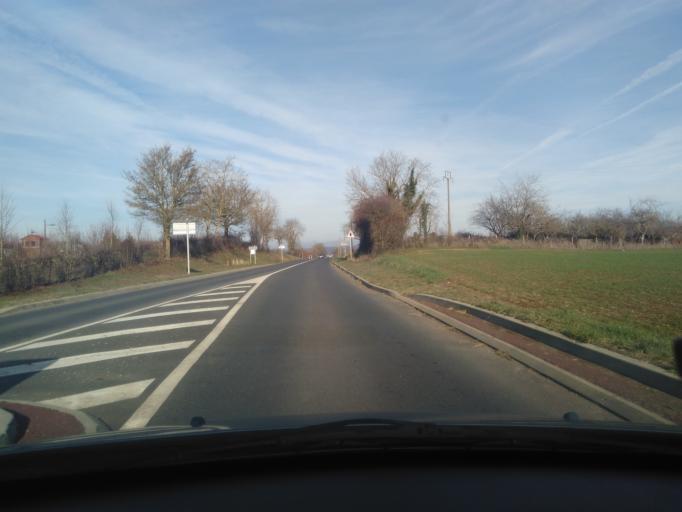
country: FR
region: Centre
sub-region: Departement du Cher
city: Orval
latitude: 46.7051
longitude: 2.4783
